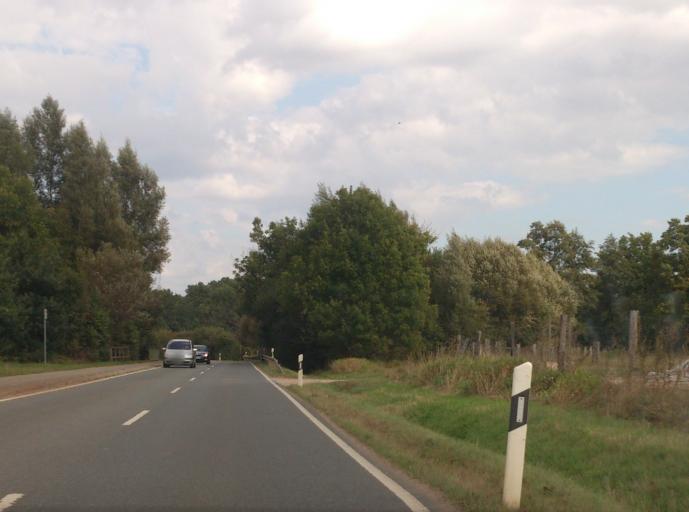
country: DE
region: Bavaria
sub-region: Regierungsbezirk Mittelfranken
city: Wetzendorf
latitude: 49.5237
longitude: 11.0575
